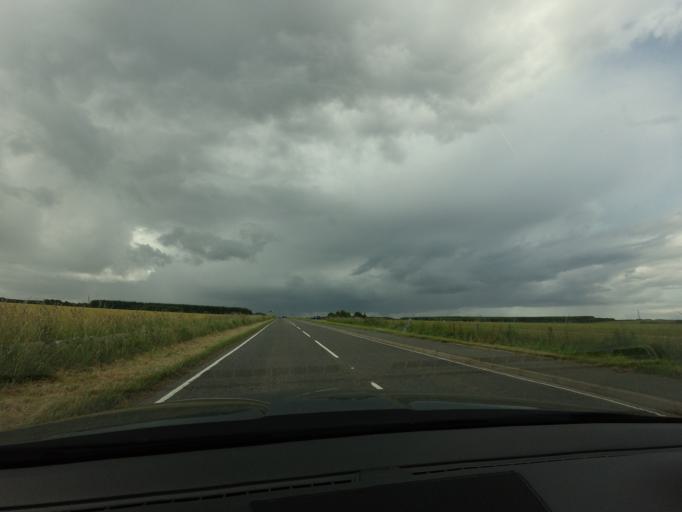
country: GB
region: Scotland
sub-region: Moray
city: Portknockie
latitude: 57.6909
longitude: -2.8529
